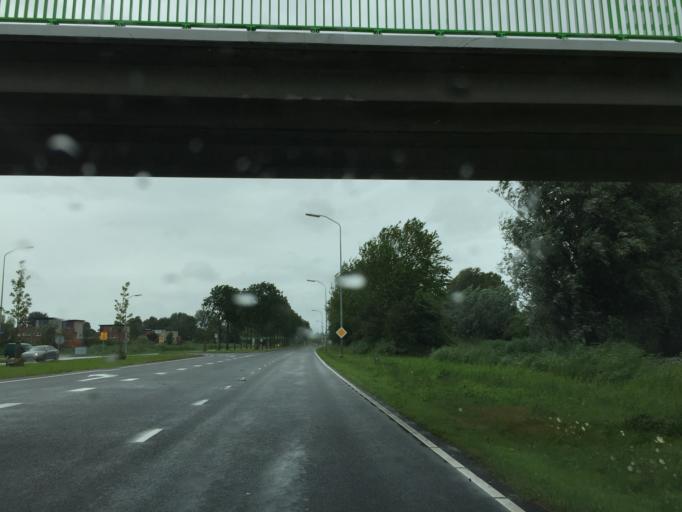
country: NL
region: Flevoland
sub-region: Gemeente Lelystad
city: Lelystad
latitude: 52.5099
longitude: 5.4522
